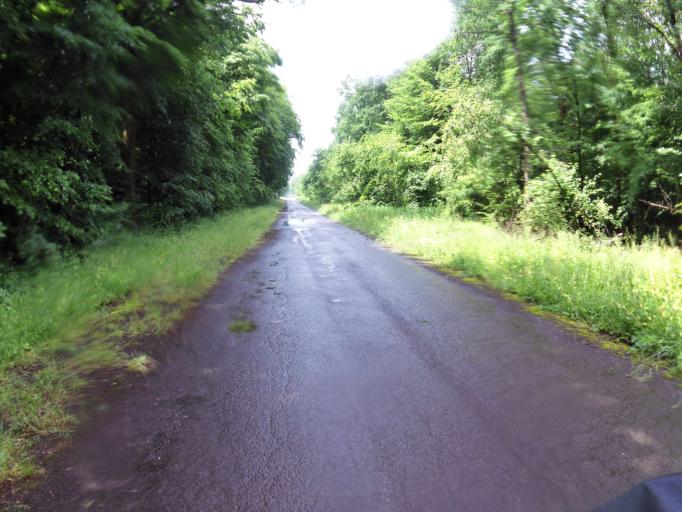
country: FR
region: Champagne-Ardenne
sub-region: Departement de la Marne
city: Sermaize-les-Bains
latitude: 48.7466
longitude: 4.9742
